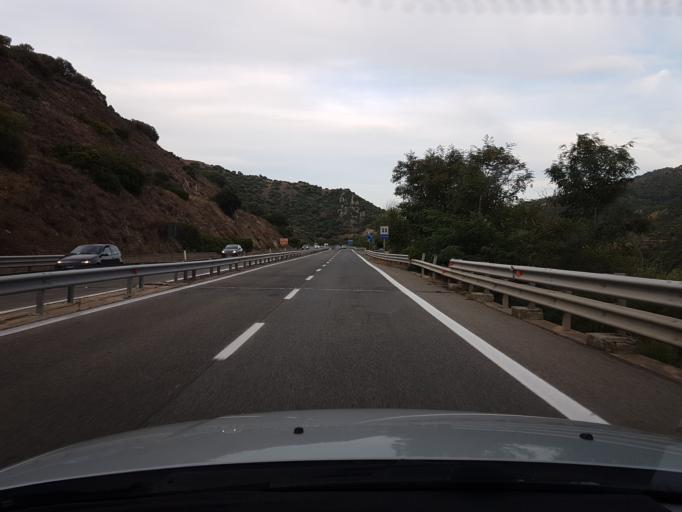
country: IT
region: Sardinia
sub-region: Provincia di Nuoro
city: Nuoro
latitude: 40.3454
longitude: 9.3244
